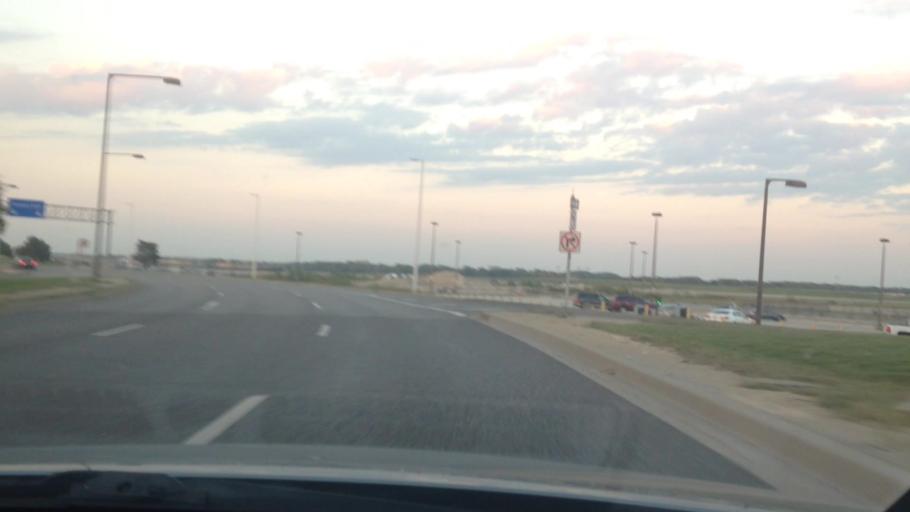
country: US
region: Missouri
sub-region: Platte County
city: Weatherby Lake
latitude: 39.2976
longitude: -94.7129
